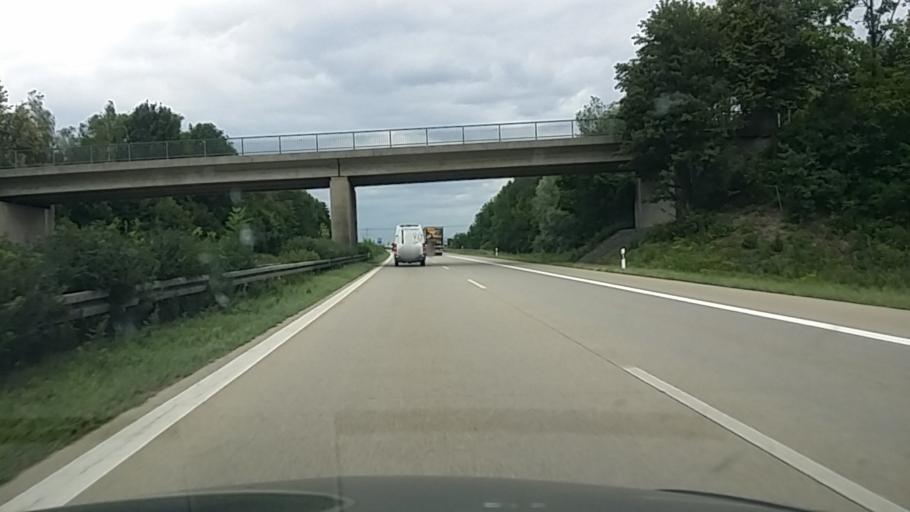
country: DE
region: Bavaria
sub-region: Lower Bavaria
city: Essenbach
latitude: 48.5909
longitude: 12.2104
